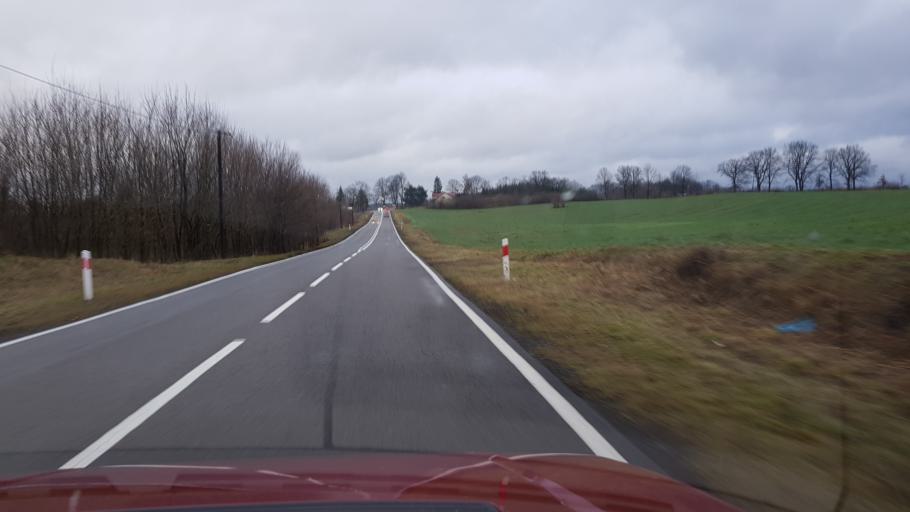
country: PL
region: West Pomeranian Voivodeship
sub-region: Powiat lobeski
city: Wegorzyno
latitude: 53.5024
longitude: 15.6620
